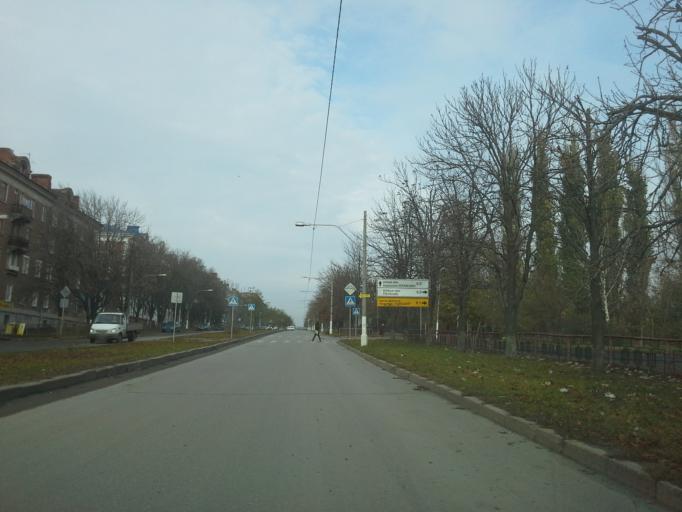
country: RU
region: Volgograd
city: Vodstroy
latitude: 48.7785
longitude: 44.5734
